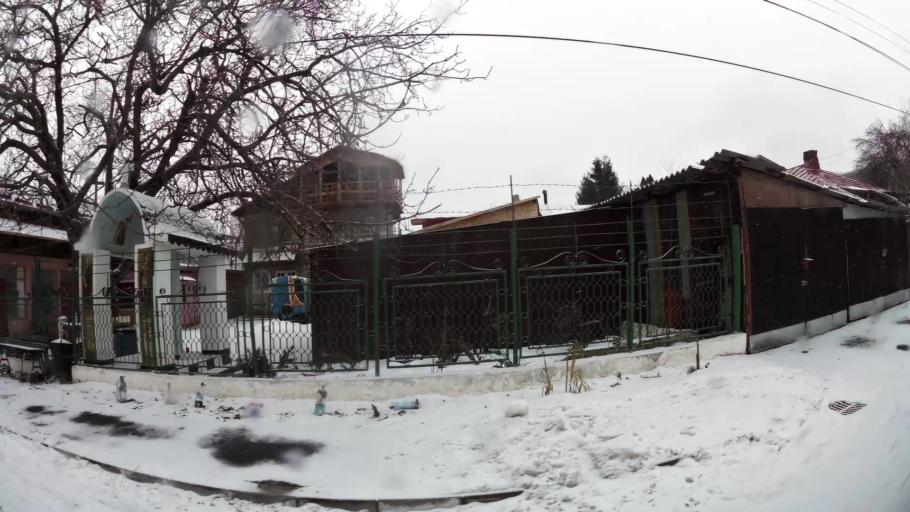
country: RO
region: Dambovita
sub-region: Municipiul Targoviste
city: Targoviste
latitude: 44.9168
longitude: 25.4622
